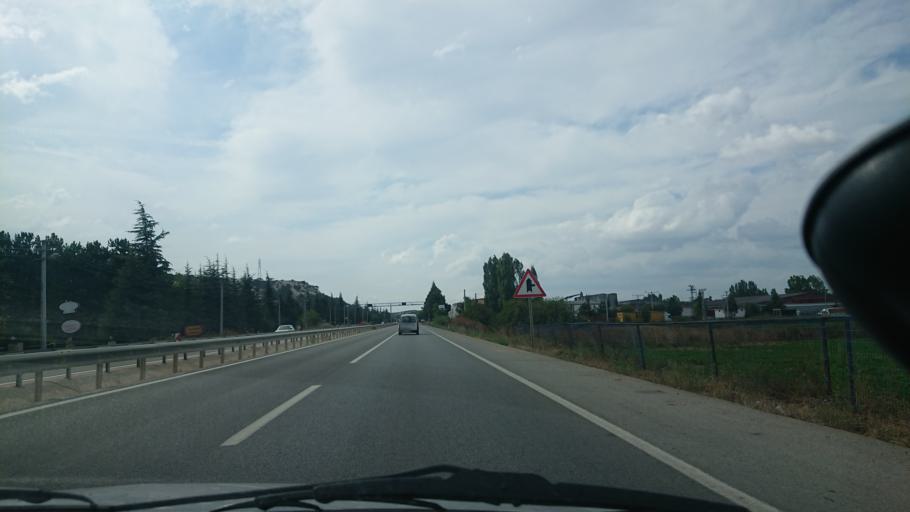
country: TR
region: Eskisehir
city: Eskisehir
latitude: 39.7270
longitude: 30.3624
